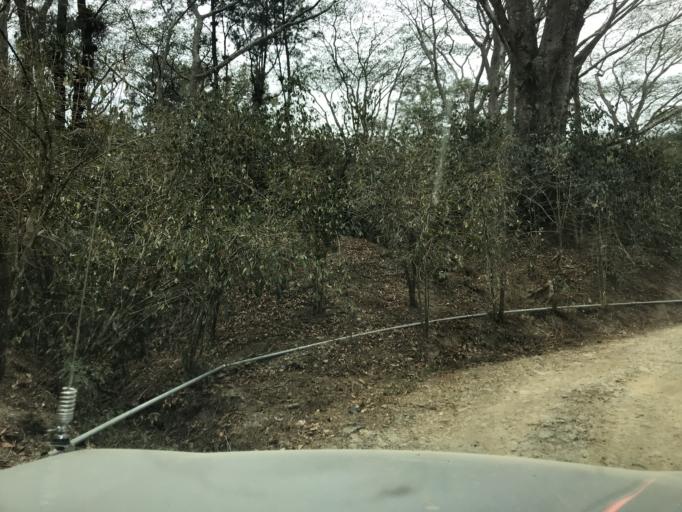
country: TL
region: Ermera
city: Gleno
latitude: -8.8362
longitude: 125.4475
